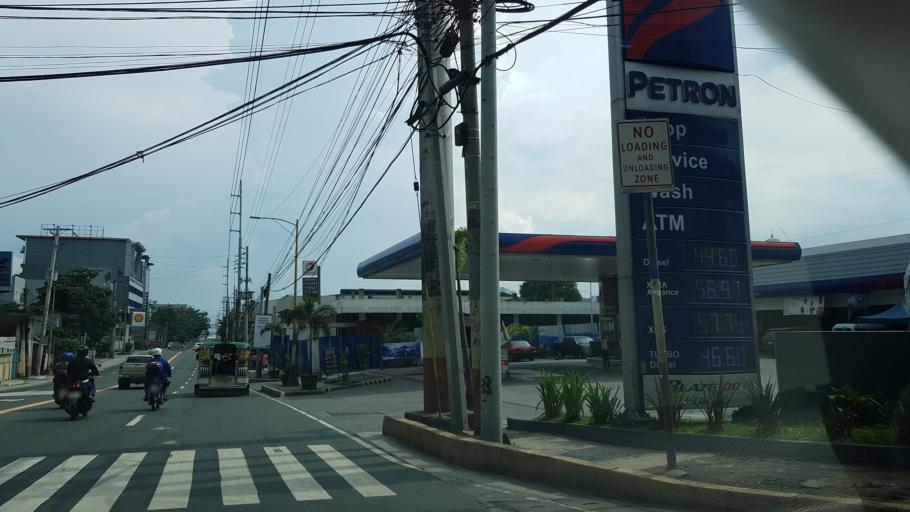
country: PH
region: Metro Manila
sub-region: Pasig
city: Pasig City
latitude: 14.5674
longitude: 121.0660
